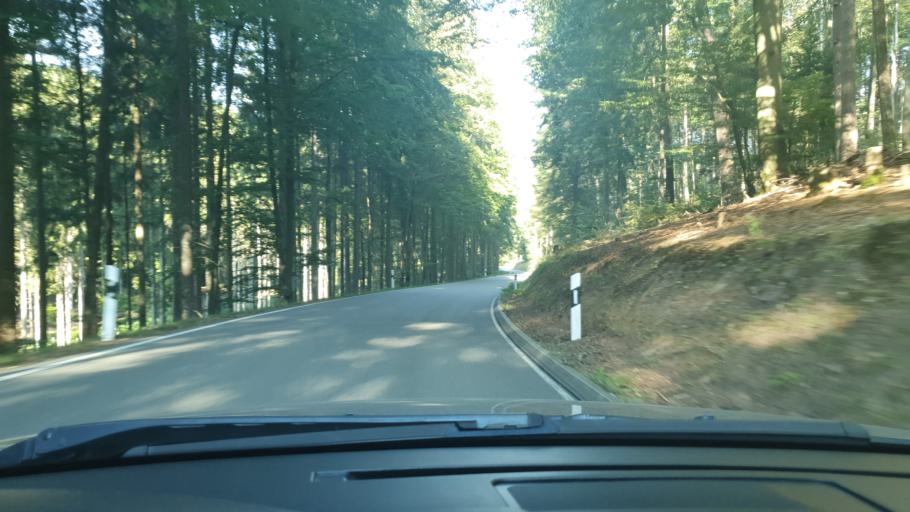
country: DE
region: Rheinland-Pfalz
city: Schmalenberg
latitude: 49.3299
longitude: 7.7596
